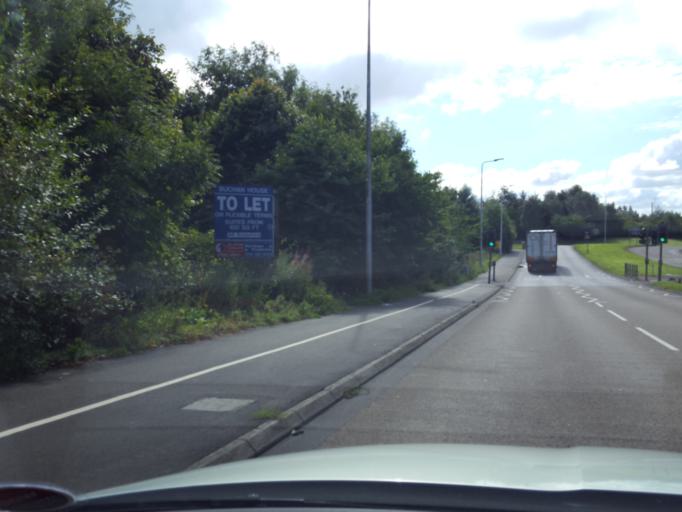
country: GB
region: Scotland
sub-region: Fife
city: Rosyth
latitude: 56.0491
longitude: -3.4305
